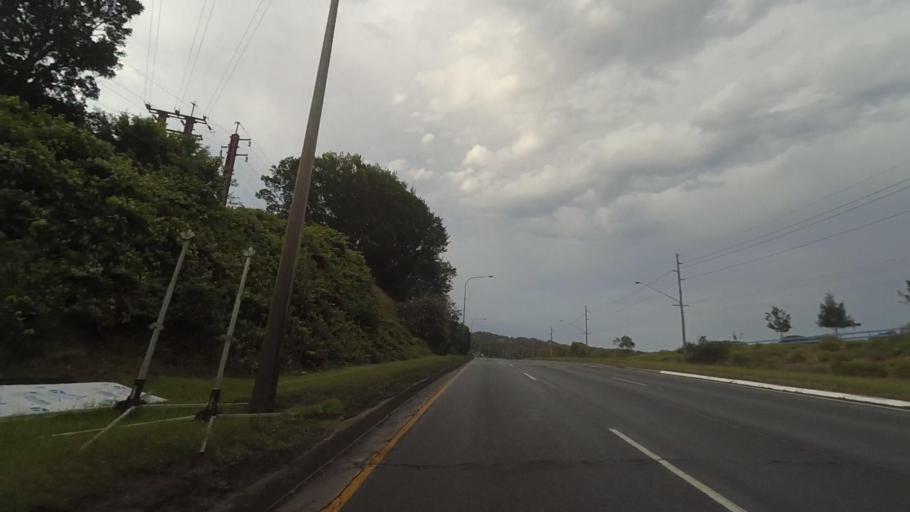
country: AU
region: New South Wales
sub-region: Wollongong
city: Mount Saint Thomas
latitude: -34.4514
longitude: 150.8743
